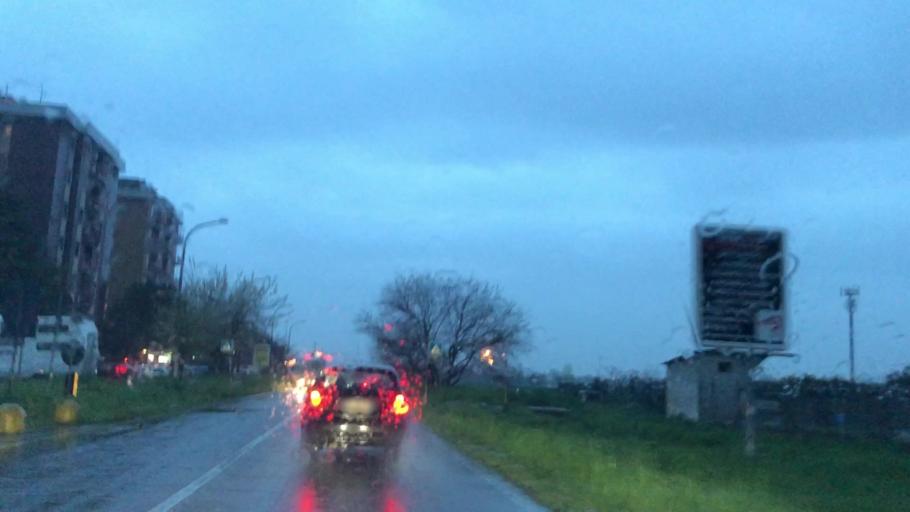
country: IT
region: Lombardy
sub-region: Citta metropolitana di Milano
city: Cusano Milanino
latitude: 45.5580
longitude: 9.1861
